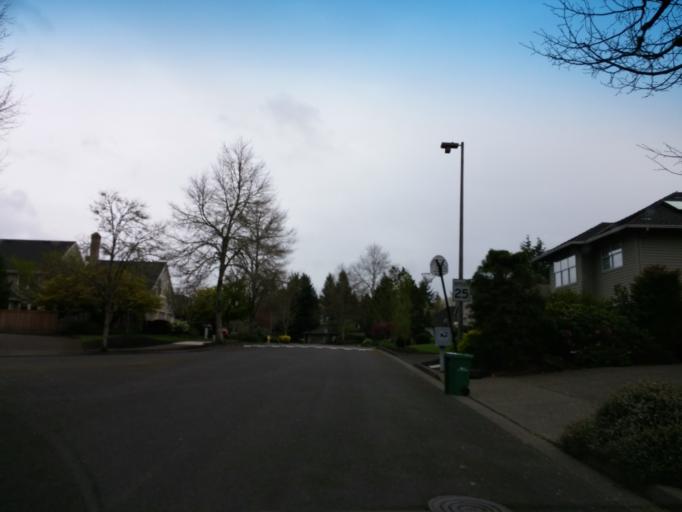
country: US
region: Oregon
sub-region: Washington County
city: Oak Hills
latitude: 45.5252
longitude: -122.8451
